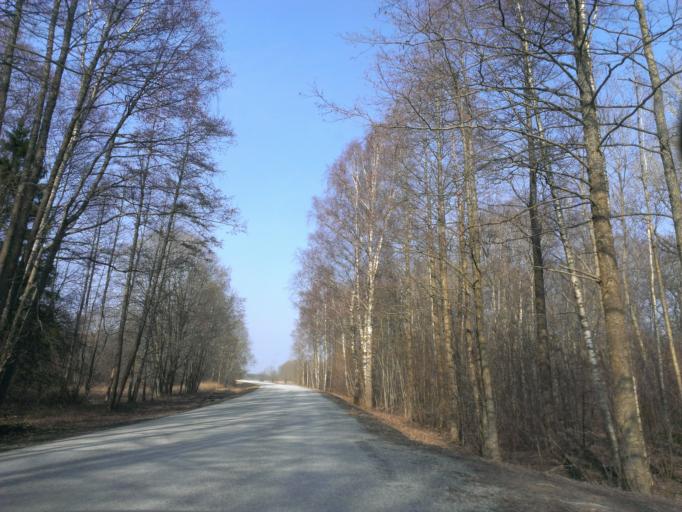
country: EE
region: Saare
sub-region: Orissaare vald
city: Orissaare
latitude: 58.5252
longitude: 23.1101
